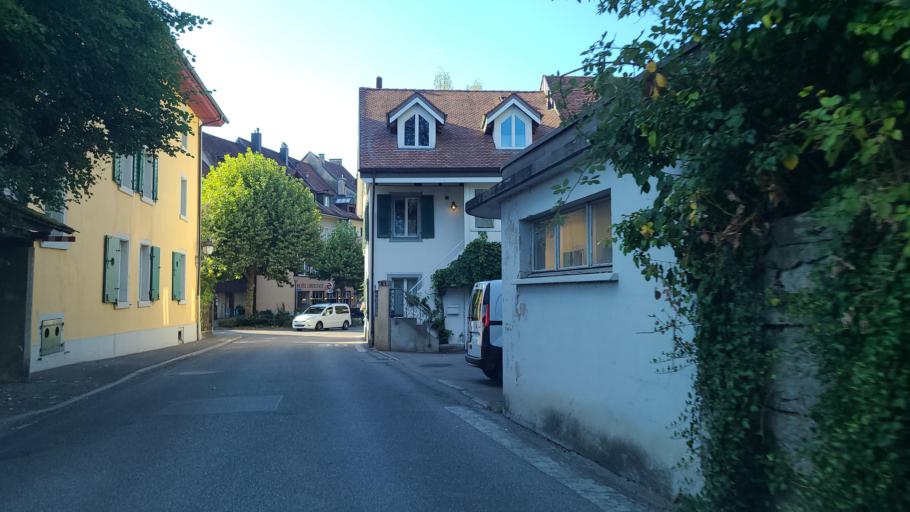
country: CH
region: Aargau
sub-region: Bezirk Lenzburg
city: Lenzburg
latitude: 47.3864
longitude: 8.1821
